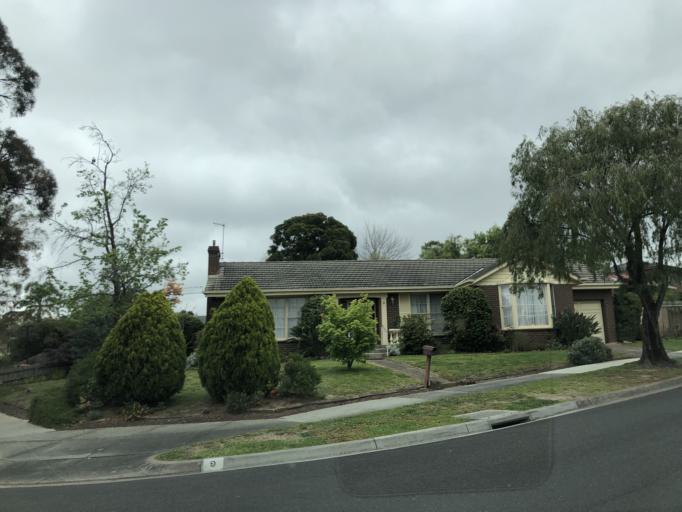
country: AU
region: Victoria
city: Burwood East
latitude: -37.8623
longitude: 145.1643
